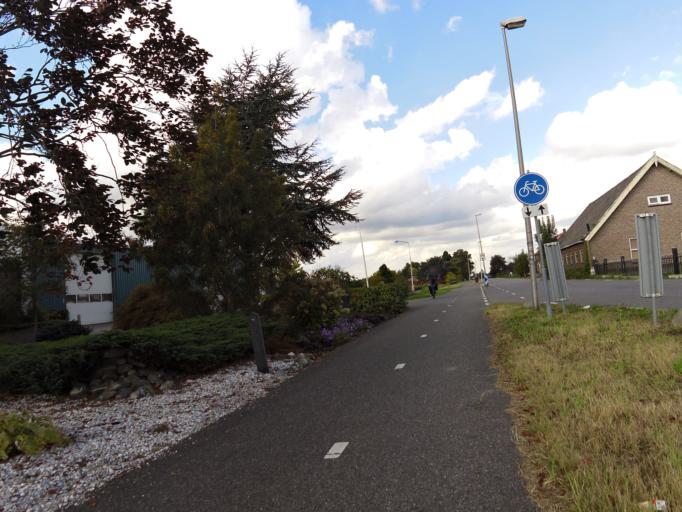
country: NL
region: South Holland
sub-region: Gemeente Boskoop
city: Boskoop
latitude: 52.0825
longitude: 4.6323
